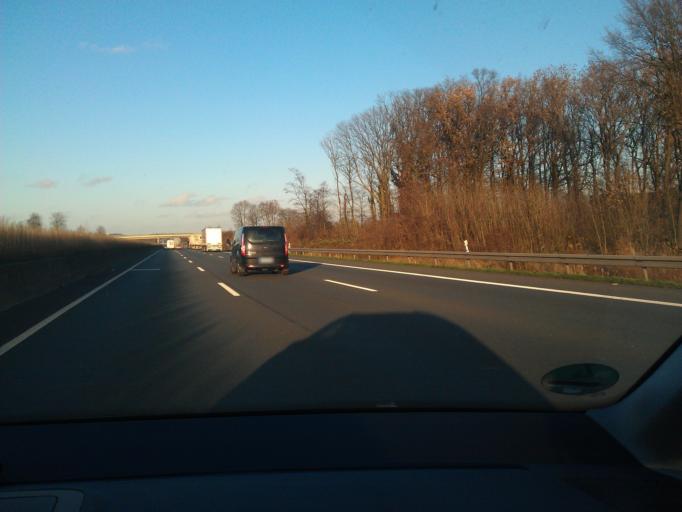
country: DE
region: North Rhine-Westphalia
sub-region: Regierungsbezirk Munster
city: Beckum
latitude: 51.7427
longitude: 7.9913
